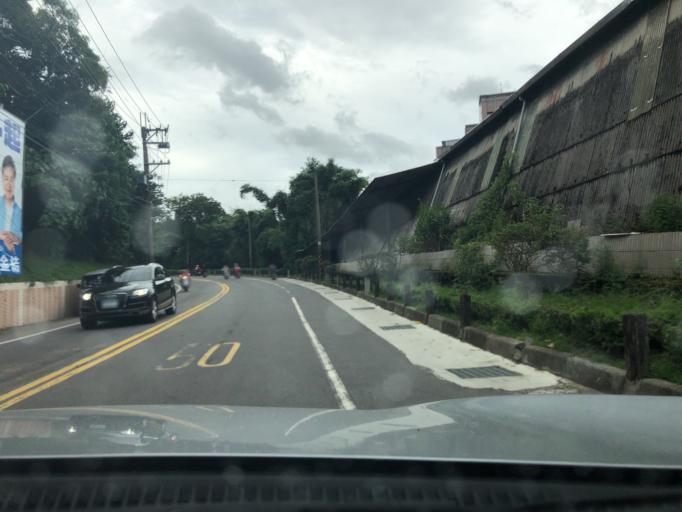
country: TW
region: Taiwan
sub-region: Taoyuan
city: Taoyuan
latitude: 24.9435
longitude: 121.3397
